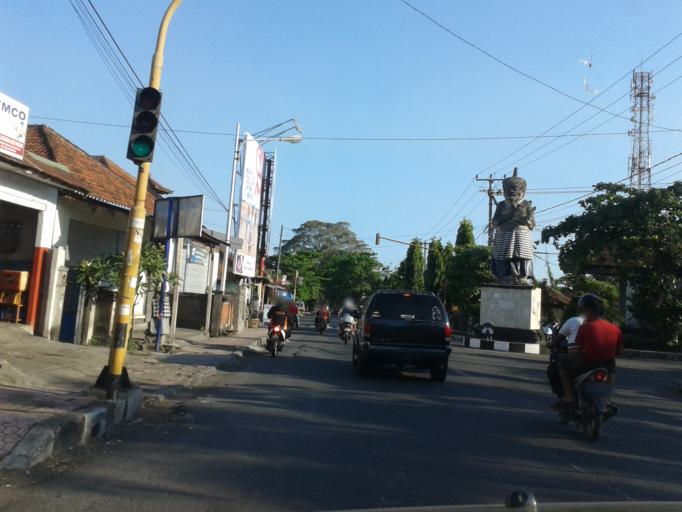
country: ID
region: Bali
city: Klungkung
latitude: -8.5248
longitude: 115.4031
